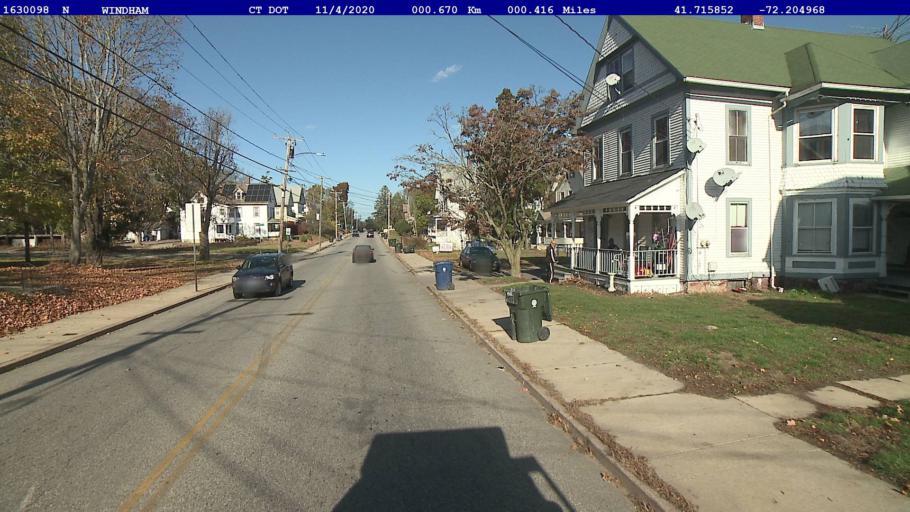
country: US
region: Connecticut
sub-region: Windham County
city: Willimantic
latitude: 41.7159
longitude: -72.2050
